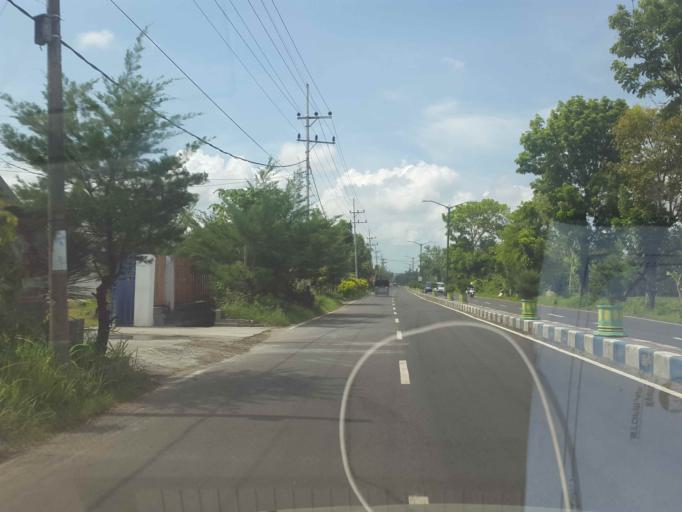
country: ID
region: East Java
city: Sumenep
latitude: -7.0405
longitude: 113.8480
